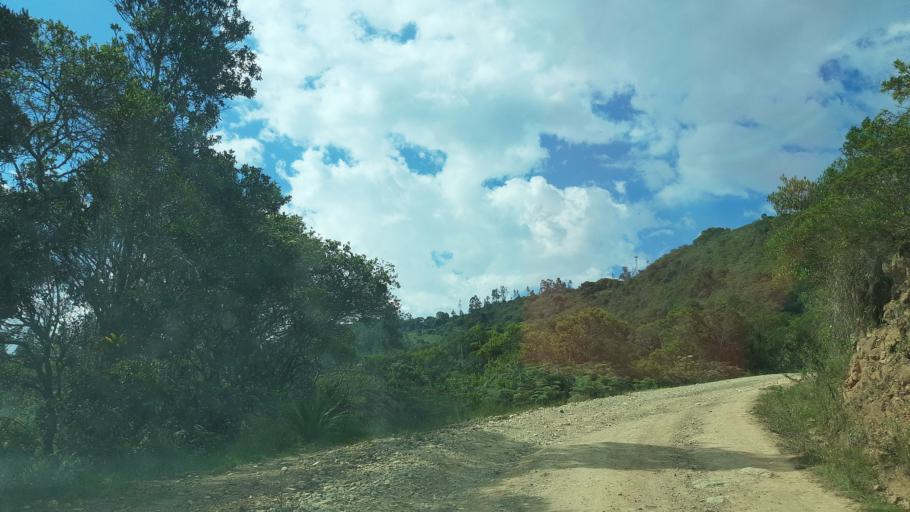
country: CO
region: Boyaca
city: Santa Sofia
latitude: 5.7240
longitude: -73.5449
